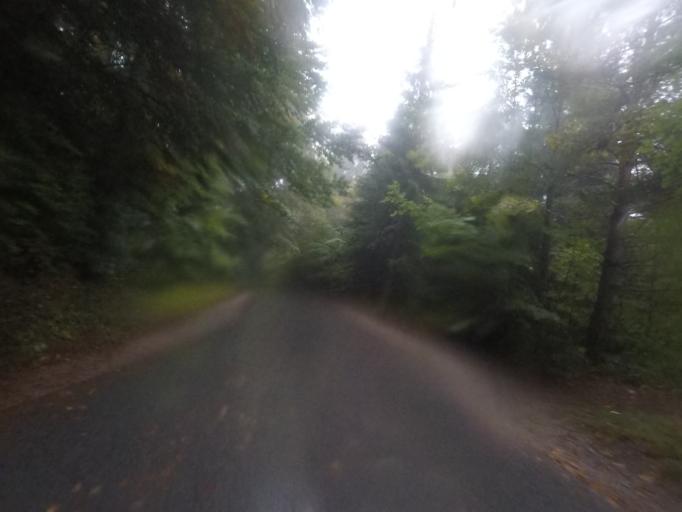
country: HR
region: Licko-Senjska
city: Jezerce
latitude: 44.9389
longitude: 15.5441
